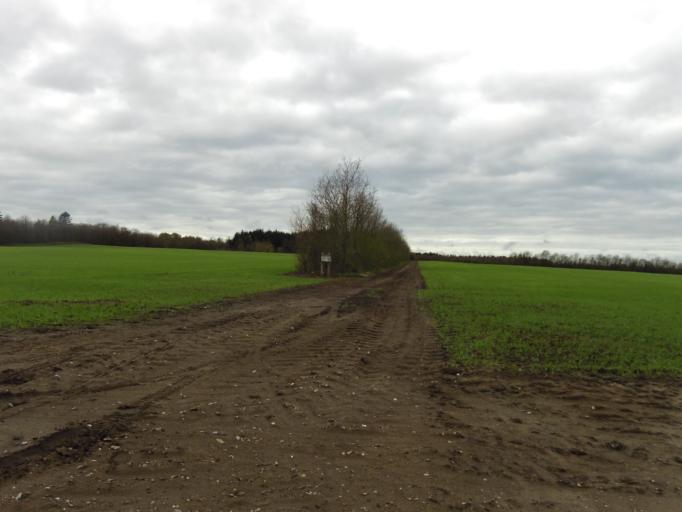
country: DK
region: South Denmark
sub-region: Esbjerg Kommune
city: Ribe
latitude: 55.3175
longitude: 8.8776
